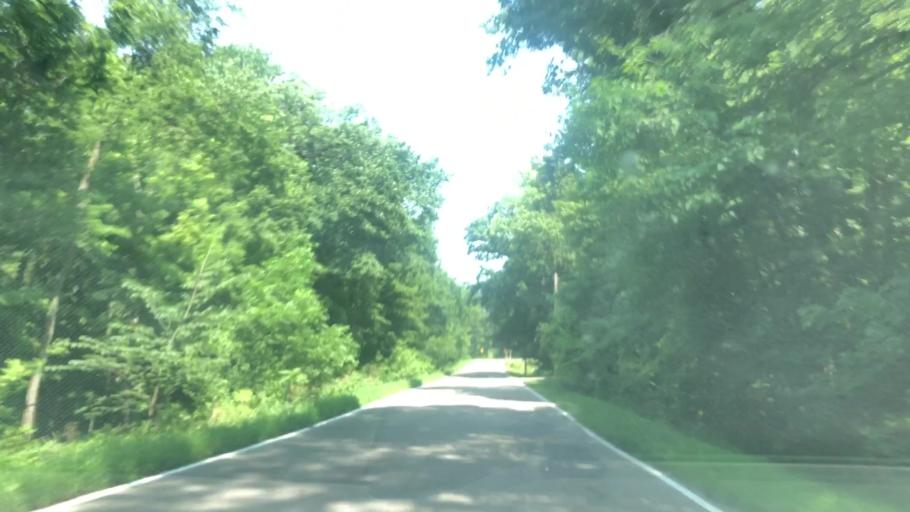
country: US
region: Iowa
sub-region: Marshall County
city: Marshalltown
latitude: 42.0268
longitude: -92.9459
